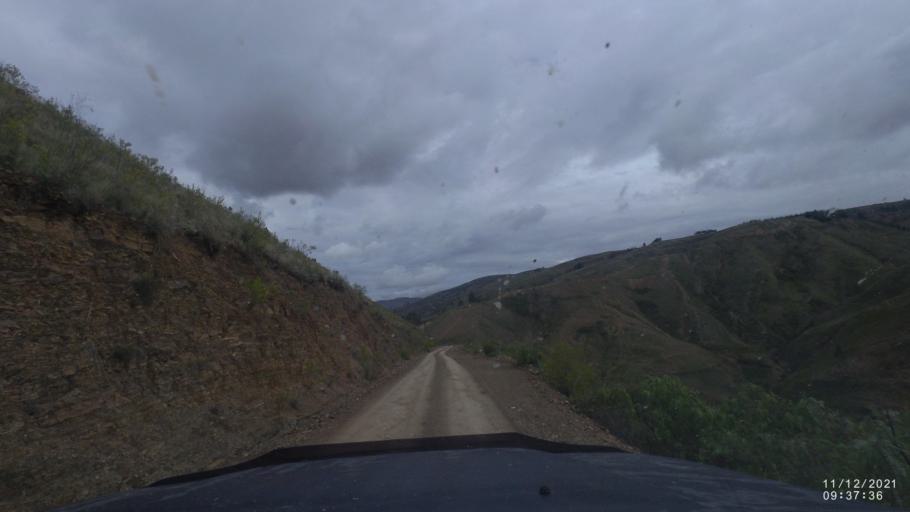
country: BO
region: Cochabamba
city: Tarata
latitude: -17.8223
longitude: -65.9857
